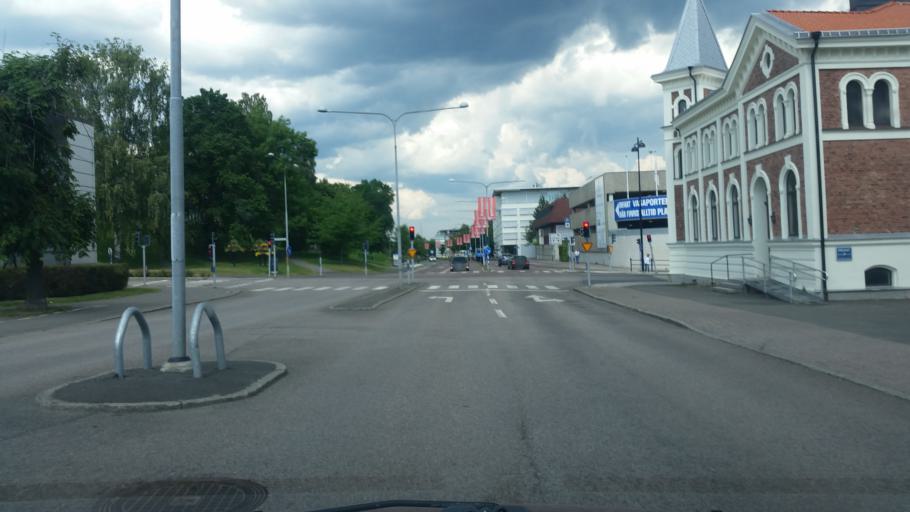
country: SE
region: Vaestra Goetaland
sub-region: Skovde Kommun
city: Skoevde
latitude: 58.3876
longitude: 13.8417
